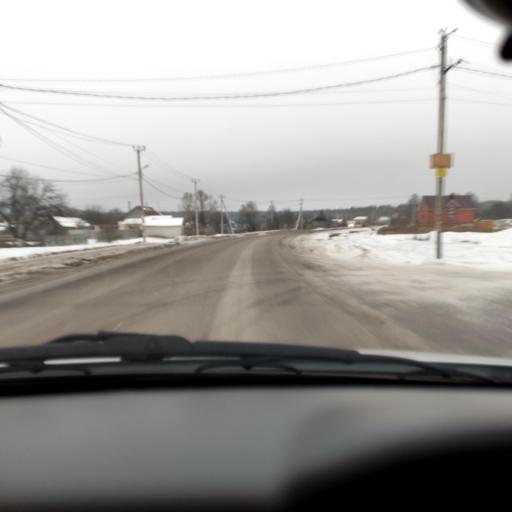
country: RU
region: Voronezj
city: Ramon'
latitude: 51.9107
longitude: 39.2871
